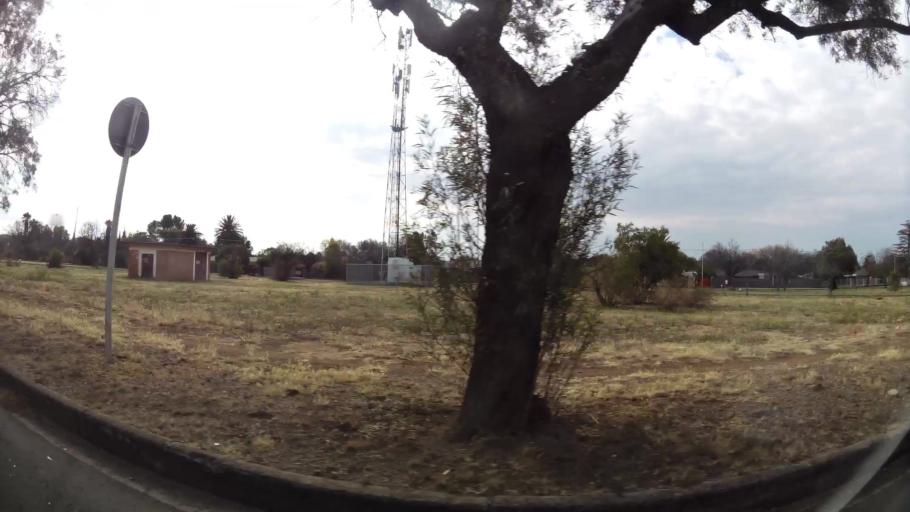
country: ZA
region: Orange Free State
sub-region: Mangaung Metropolitan Municipality
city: Bloemfontein
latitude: -29.0902
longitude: 26.2427
